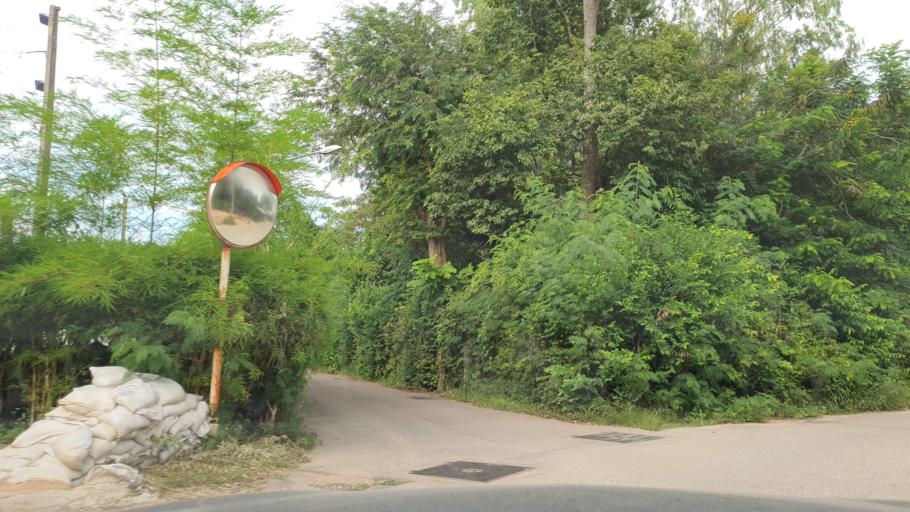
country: TH
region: Chon Buri
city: Phatthaya
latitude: 12.9558
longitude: 100.9146
